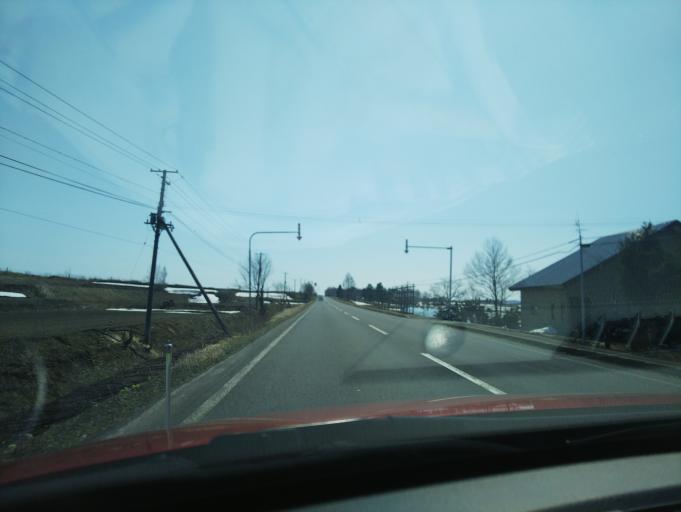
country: JP
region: Hokkaido
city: Nayoro
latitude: 44.2592
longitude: 142.3946
